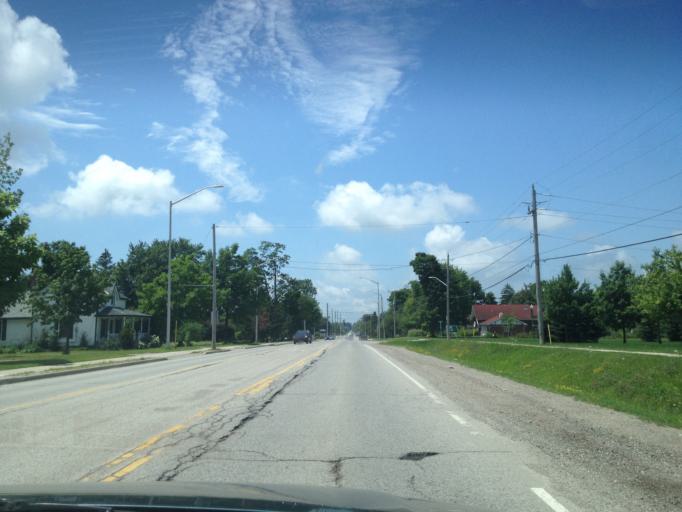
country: CA
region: Ontario
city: London
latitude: 43.0004
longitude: -81.3267
